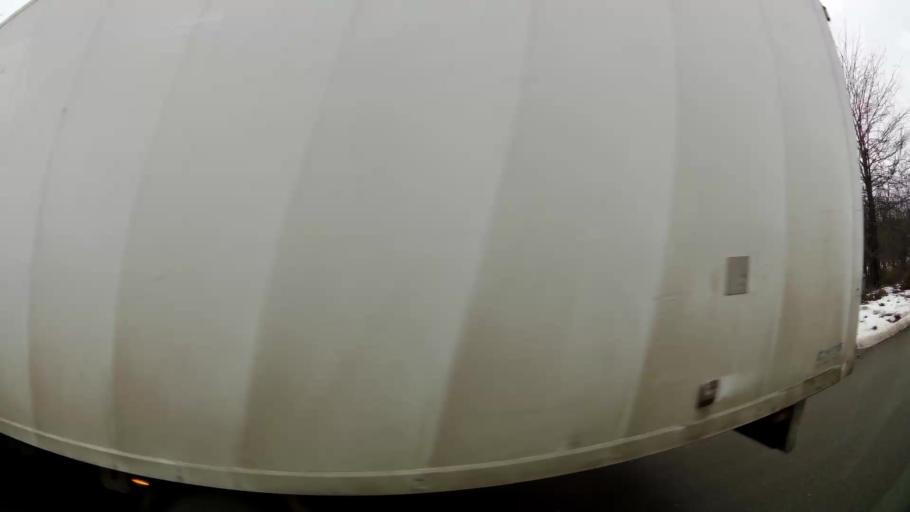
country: RO
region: Ilfov
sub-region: Comuna Chitila
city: Chitila
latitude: 44.5012
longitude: 26.0072
